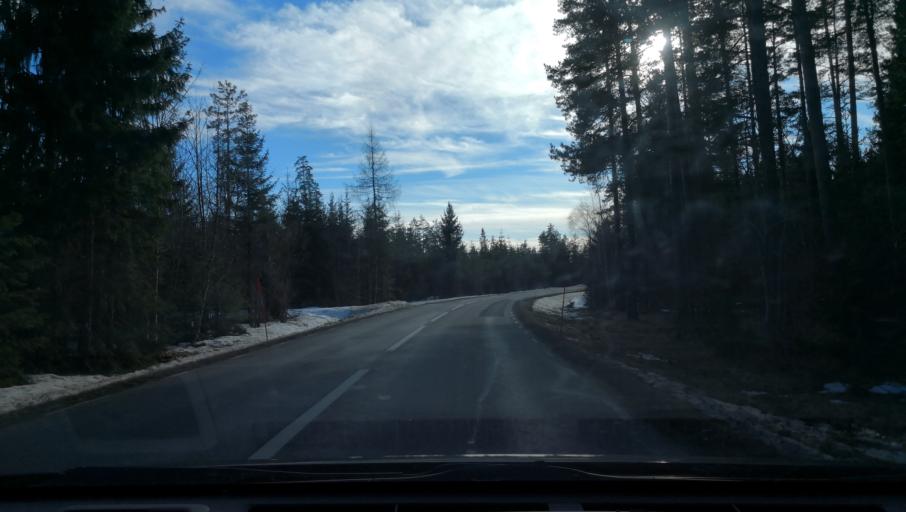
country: SE
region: Uppsala
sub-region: Osthammars Kommun
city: Osterbybruk
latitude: 60.2606
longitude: 17.9512
